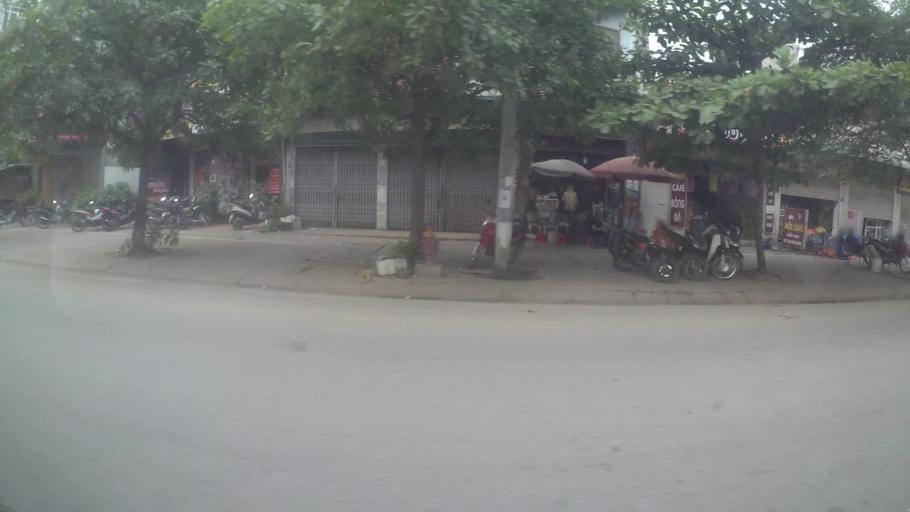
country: VN
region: Ha Noi
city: Cau Dien
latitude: 21.0475
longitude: 105.7464
